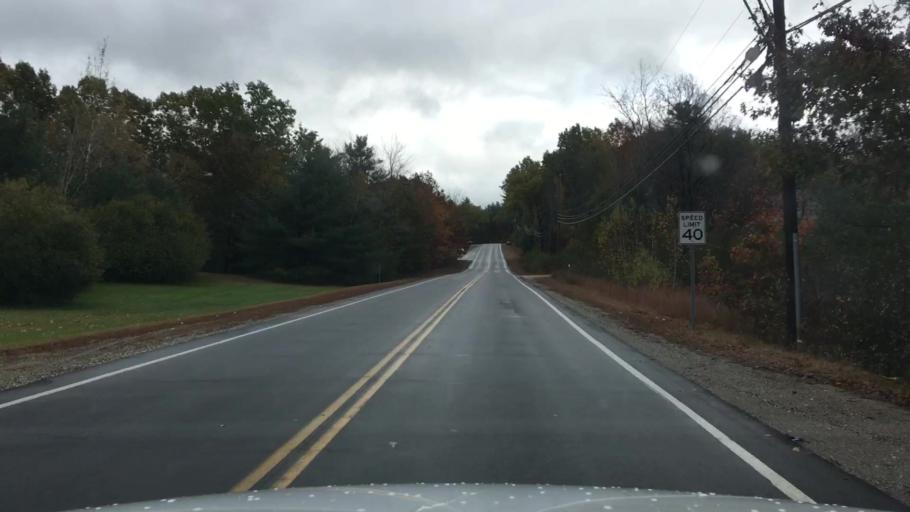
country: US
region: New Hampshire
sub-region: Strafford County
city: Lee
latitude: 43.1288
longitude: -71.0225
